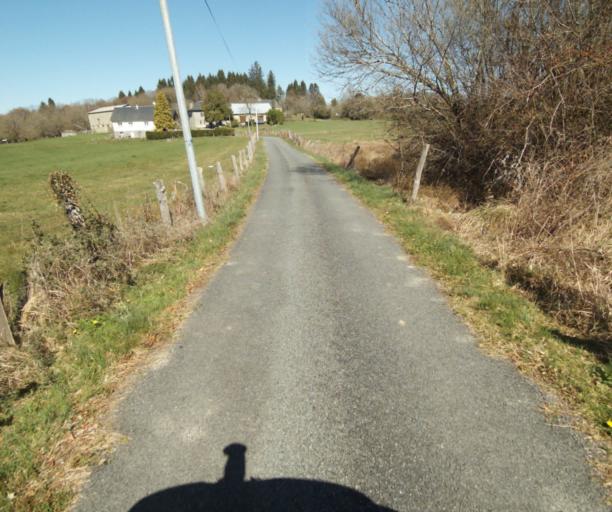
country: FR
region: Limousin
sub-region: Departement de la Correze
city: Saint-Mexant
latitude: 45.2758
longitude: 1.6755
